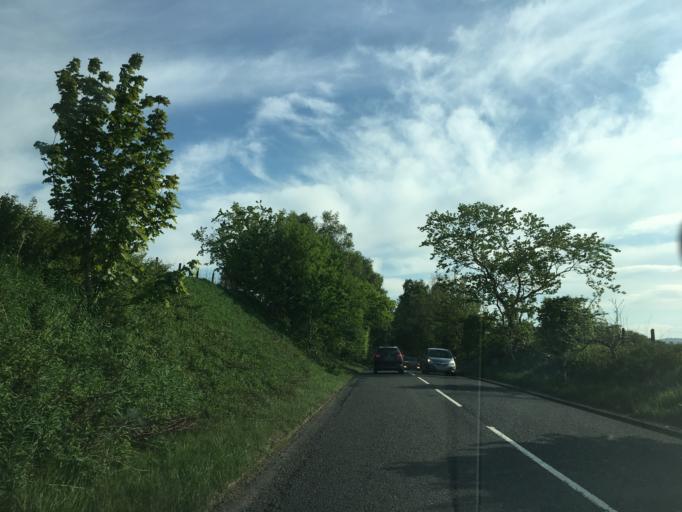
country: GB
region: Scotland
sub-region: The Scottish Borders
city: West Linton
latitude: 55.6820
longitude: -3.4005
